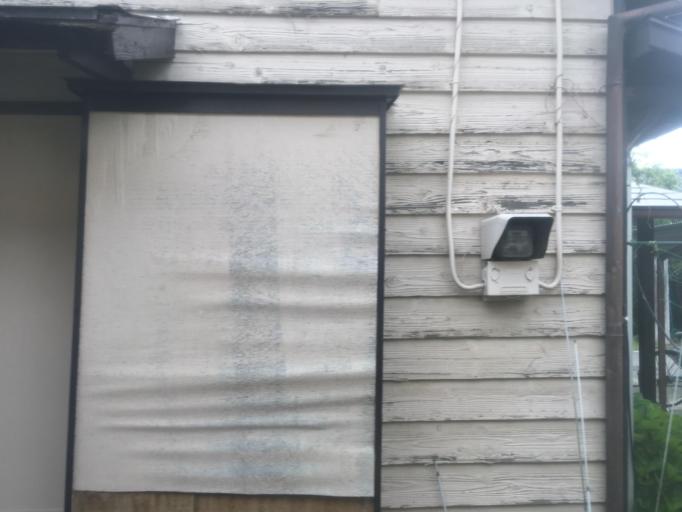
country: JP
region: Gunma
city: Yoshii
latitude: 36.2616
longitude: 139.0095
